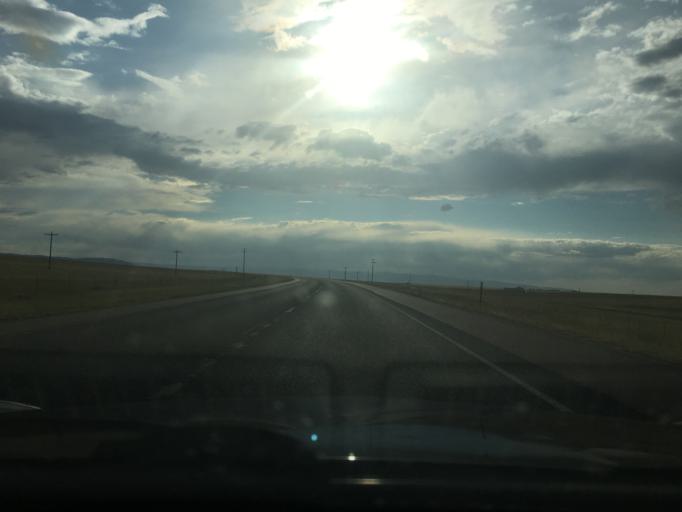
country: US
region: Wyoming
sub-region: Albany County
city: Laramie
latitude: 41.3288
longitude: -105.6858
